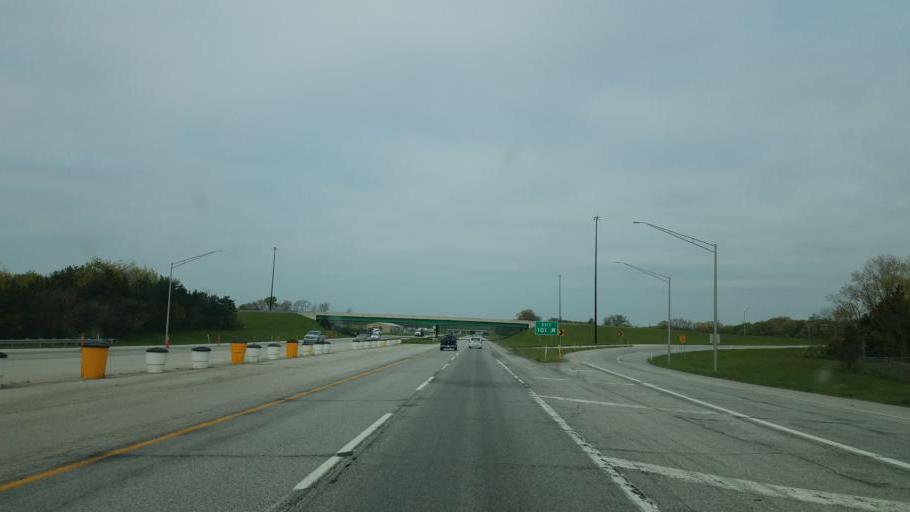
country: US
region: Indiana
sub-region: Elkhart County
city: Bristol
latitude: 41.7354
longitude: -85.7871
